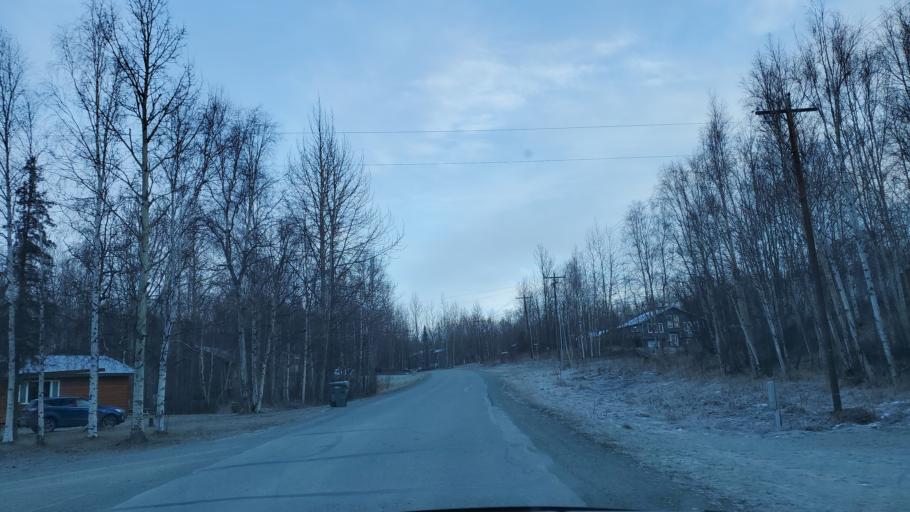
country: US
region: Alaska
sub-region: Matanuska-Susitna Borough
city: Lakes
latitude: 61.6110
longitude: -149.3086
